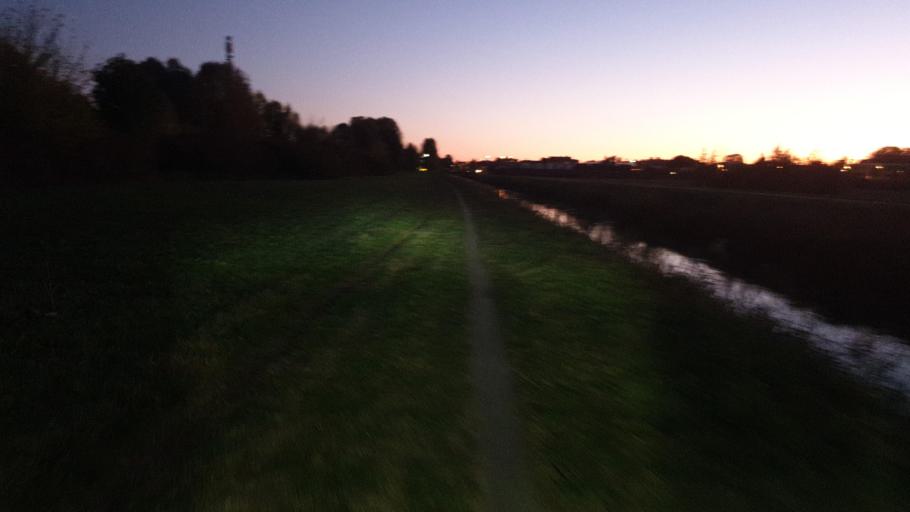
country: IT
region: Veneto
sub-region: Provincia di Venezia
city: Stra
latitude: 45.4194
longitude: 12.0093
